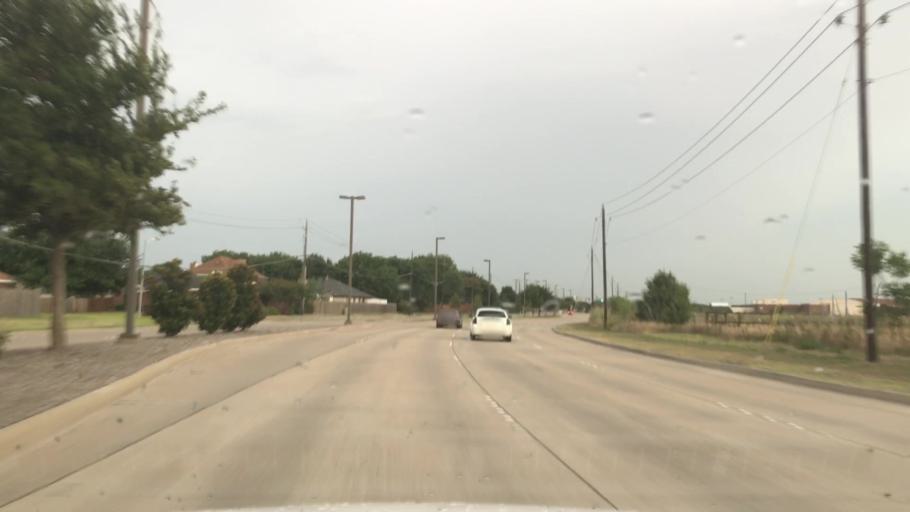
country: US
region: Texas
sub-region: Dallas County
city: Mesquite
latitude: 32.7372
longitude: -96.5621
